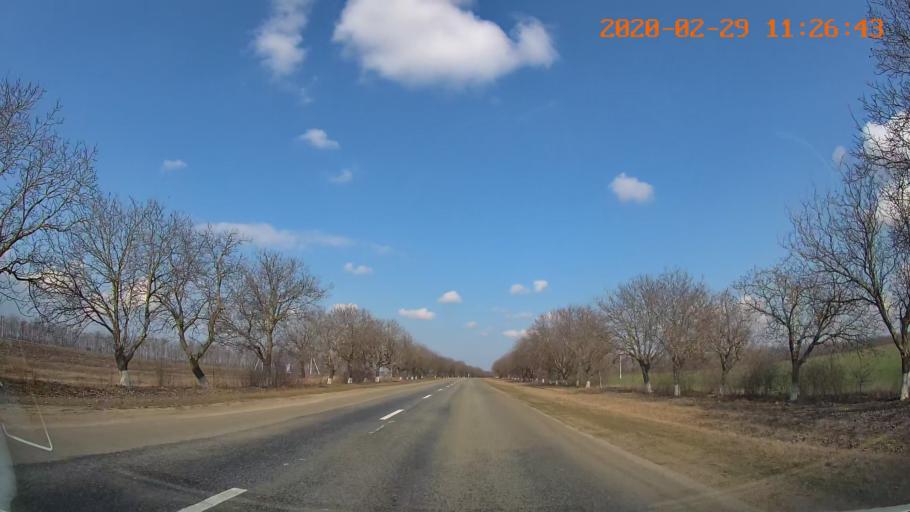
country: MD
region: Telenesti
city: Cocieri
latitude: 47.4572
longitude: 29.1449
